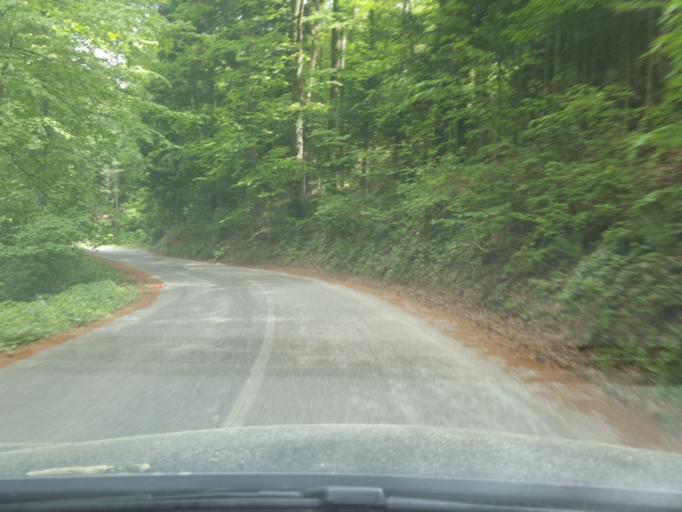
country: RS
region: Central Serbia
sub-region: Zlatiborski Okrug
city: Bajina Basta
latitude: 43.9182
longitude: 19.4873
